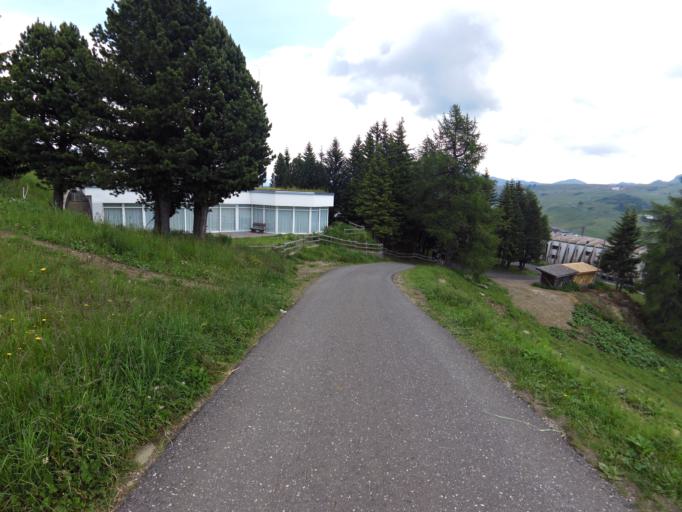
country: IT
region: Trentino-Alto Adige
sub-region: Bolzano
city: Siusi
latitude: 46.5436
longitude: 11.6146
